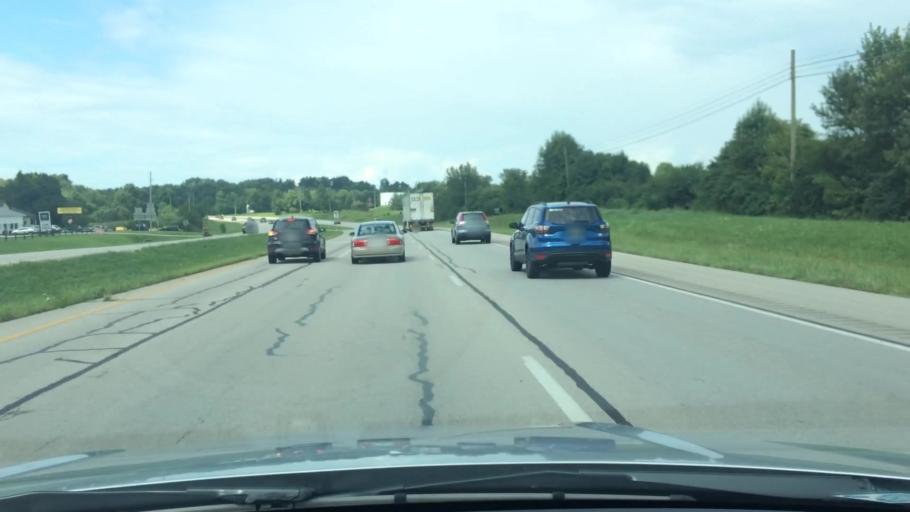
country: US
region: Kentucky
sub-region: Anderson County
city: Lawrenceburg
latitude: 38.0712
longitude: -84.9165
